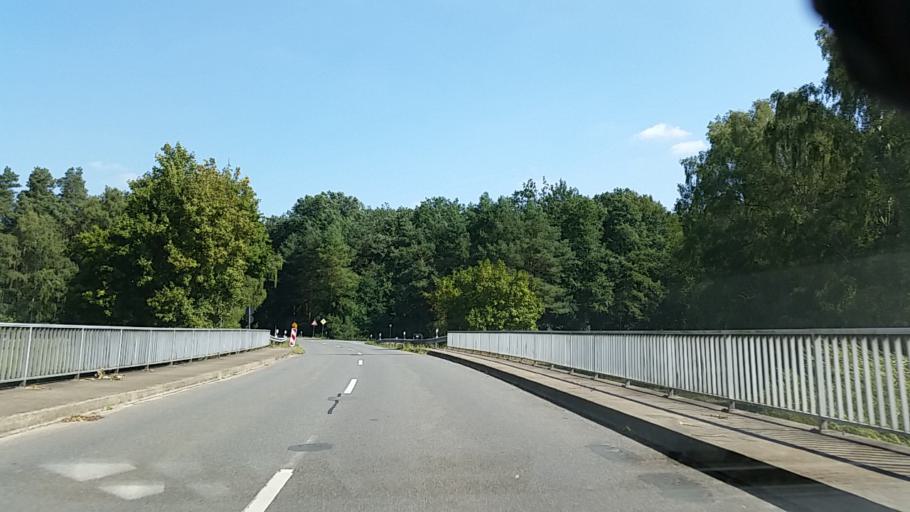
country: DE
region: Lower Saxony
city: Jelmstorf
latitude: 53.1099
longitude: 10.5457
